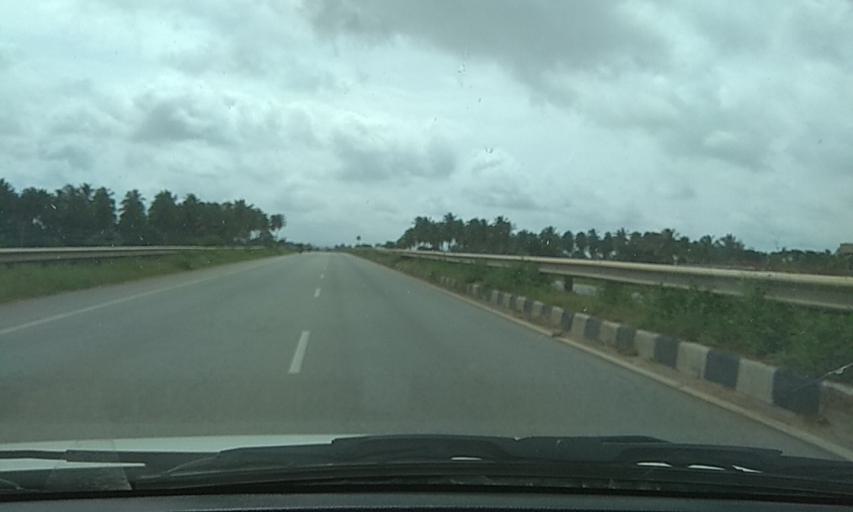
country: IN
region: Karnataka
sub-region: Davanagere
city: Harihar
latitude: 14.4521
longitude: 75.8744
